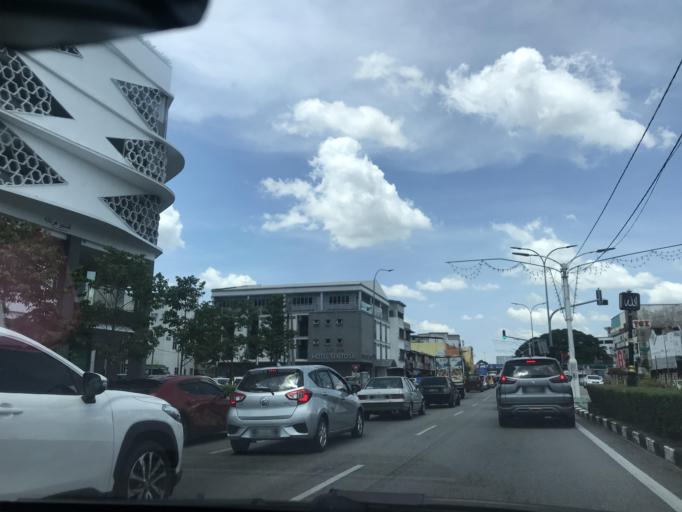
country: MY
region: Kelantan
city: Kota Bharu
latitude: 6.1207
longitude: 102.2403
